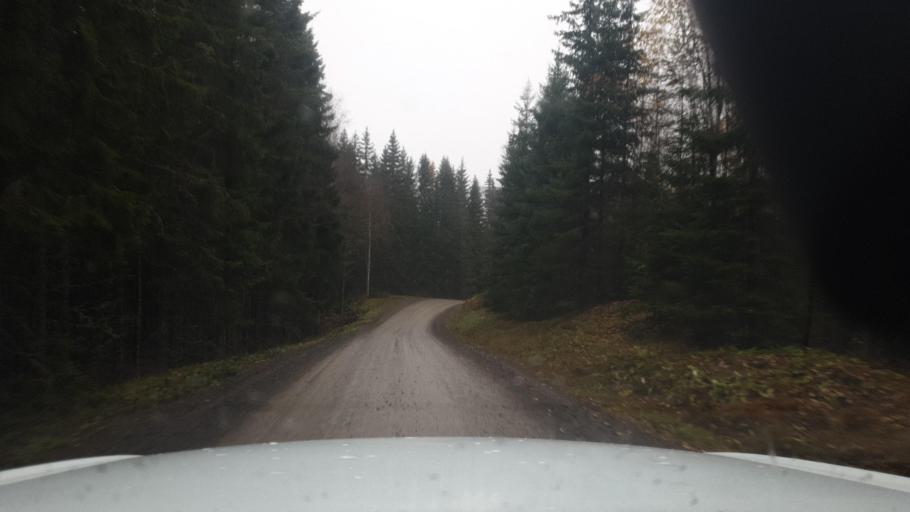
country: SE
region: Vaermland
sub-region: Arvika Kommun
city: Arvika
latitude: 59.9548
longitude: 12.6595
